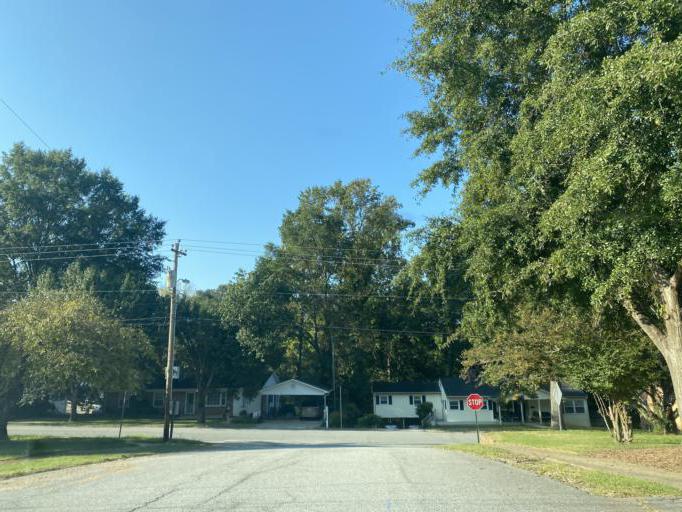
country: US
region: South Carolina
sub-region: Cherokee County
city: Gaffney
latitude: 35.0614
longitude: -81.6613
